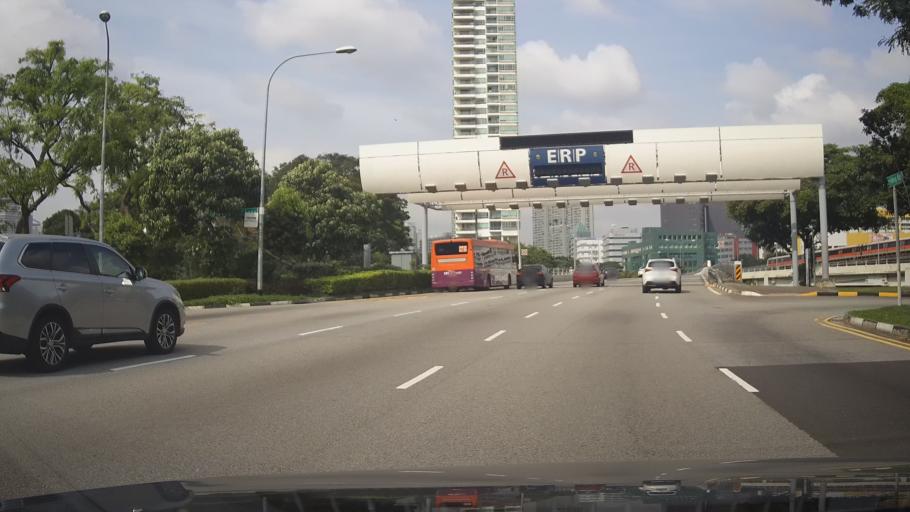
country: SG
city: Singapore
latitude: 1.3101
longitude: 103.8715
